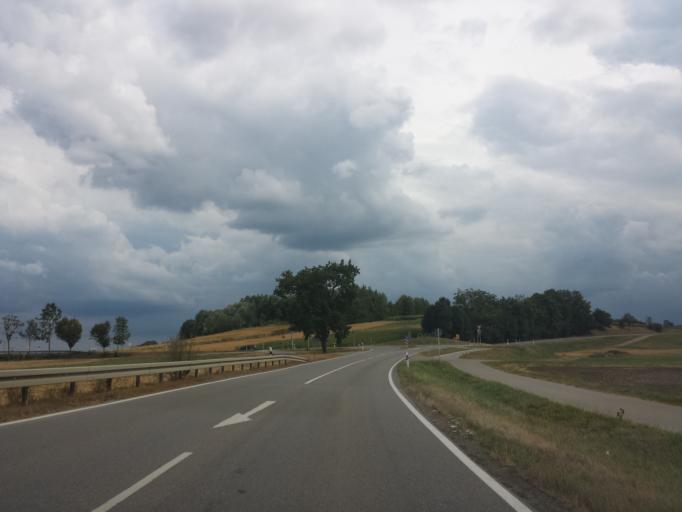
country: DE
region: Bavaria
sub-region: Swabia
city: Burgau
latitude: 48.4504
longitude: 10.3854
